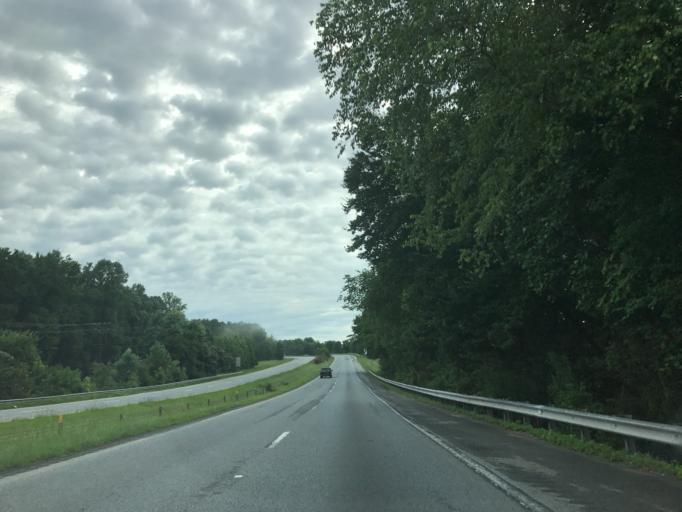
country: US
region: South Carolina
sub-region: Spartanburg County
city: Valley Falls
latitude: 35.0048
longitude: -81.9213
